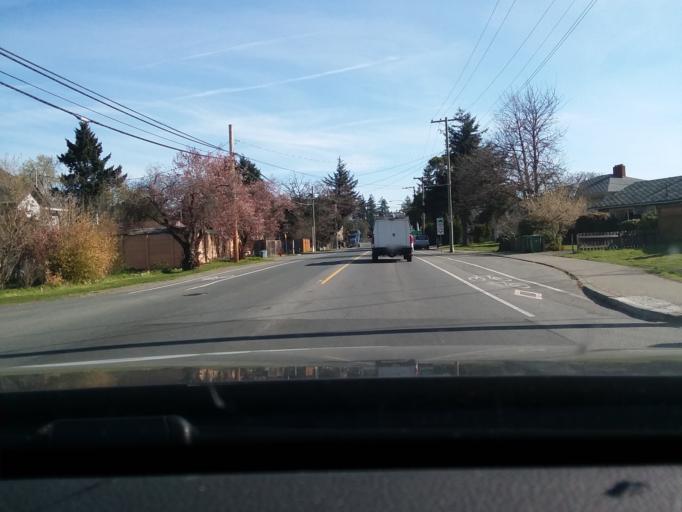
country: CA
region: British Columbia
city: Langford
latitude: 48.4318
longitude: -123.5267
